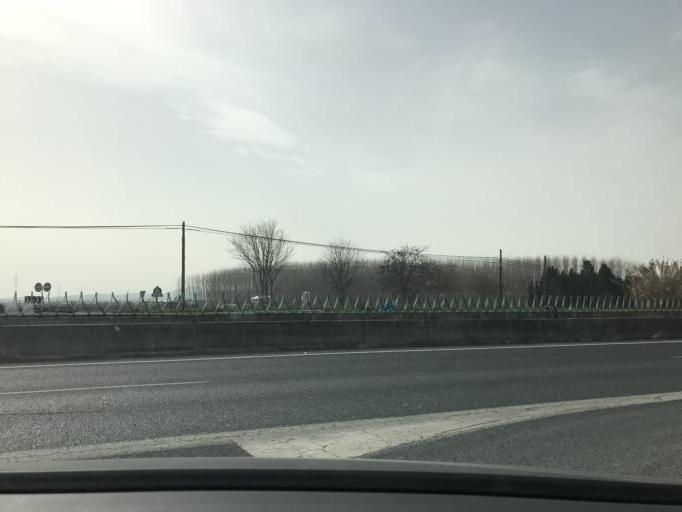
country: ES
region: Andalusia
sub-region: Provincia de Granada
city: Atarfe
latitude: 37.1925
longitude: -3.6703
